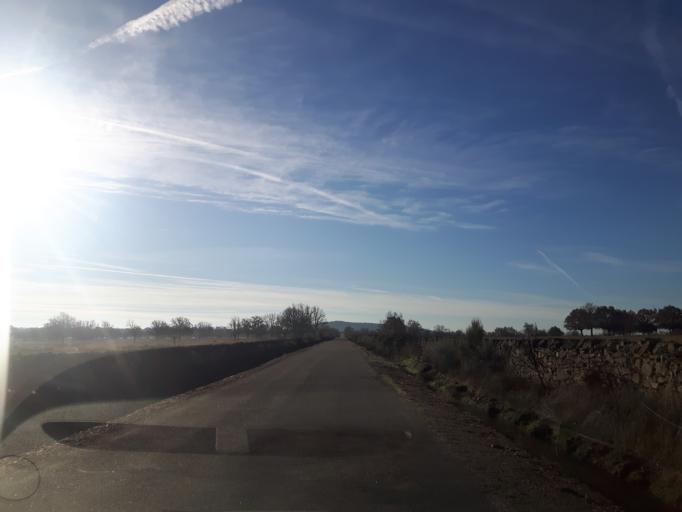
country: ES
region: Castille and Leon
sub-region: Provincia de Salamanca
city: Olmedo de Camaces
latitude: 40.9315
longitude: -6.6190
